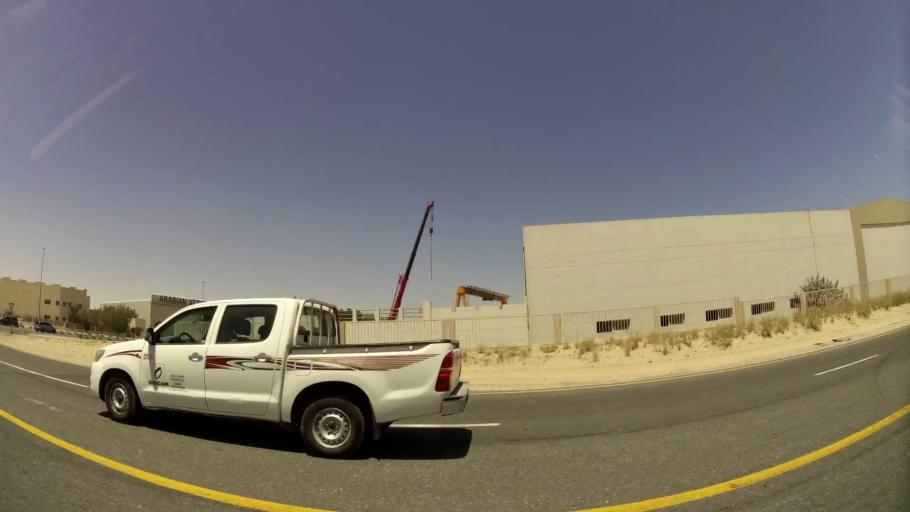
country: AE
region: Dubai
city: Dubai
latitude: 24.9734
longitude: 55.1879
